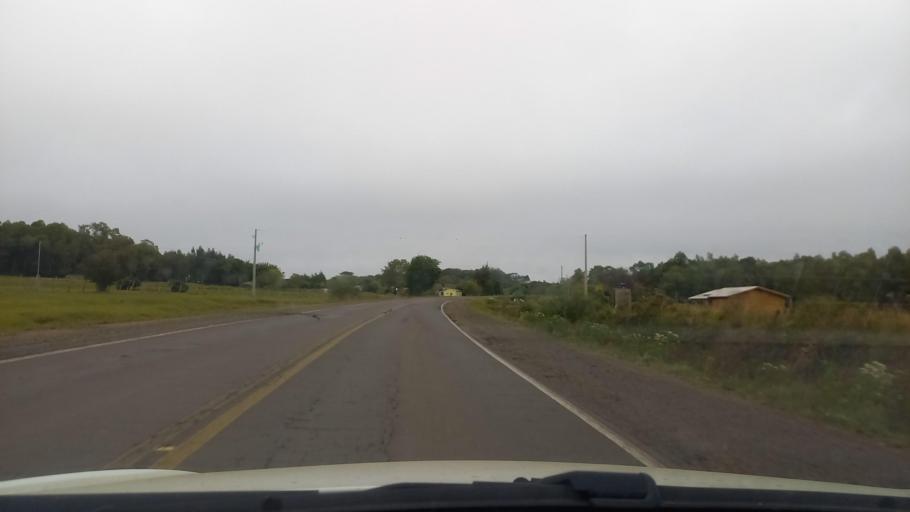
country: BR
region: Rio Grande do Sul
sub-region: Cacequi
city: Cacequi
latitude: -30.1213
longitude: -54.6394
